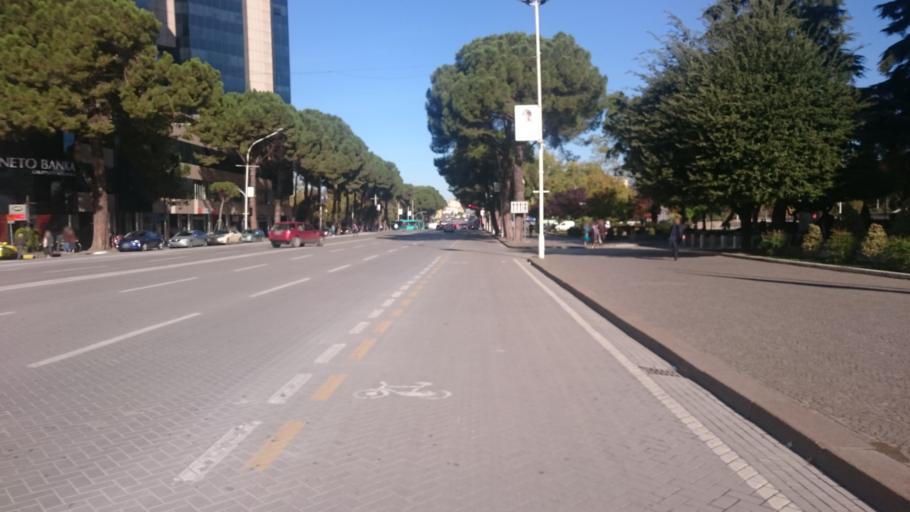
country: AL
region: Tirane
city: Tirana
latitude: 41.3217
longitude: 19.8204
